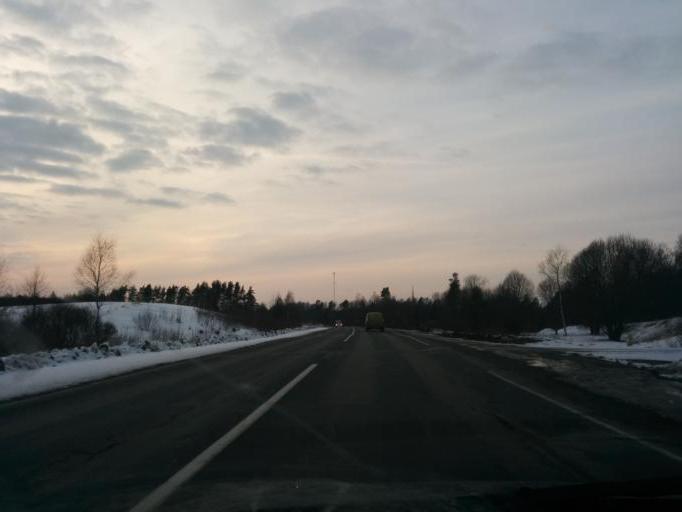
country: LV
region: Raunas
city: Rauna
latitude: 57.3194
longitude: 25.7045
